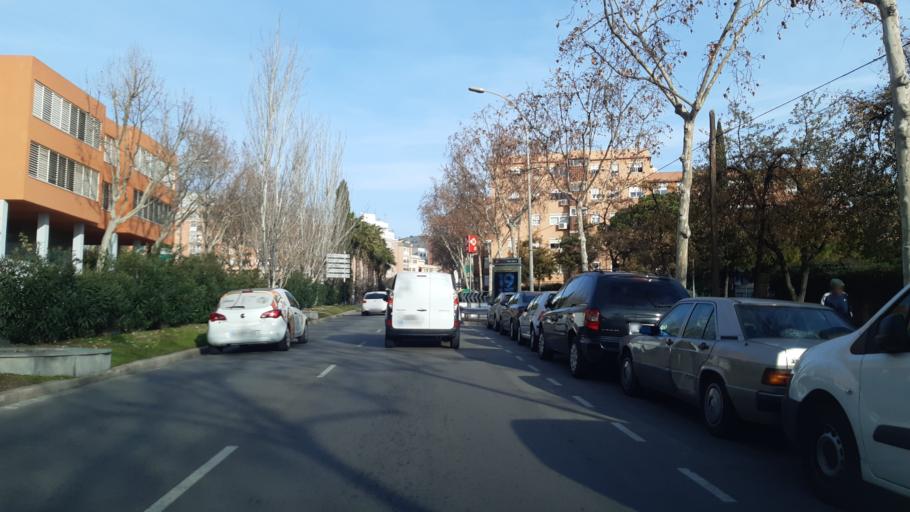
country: ES
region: Catalonia
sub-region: Provincia de Barcelona
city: L'Hospitalet de Llobregat
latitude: 41.3676
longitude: 2.1037
